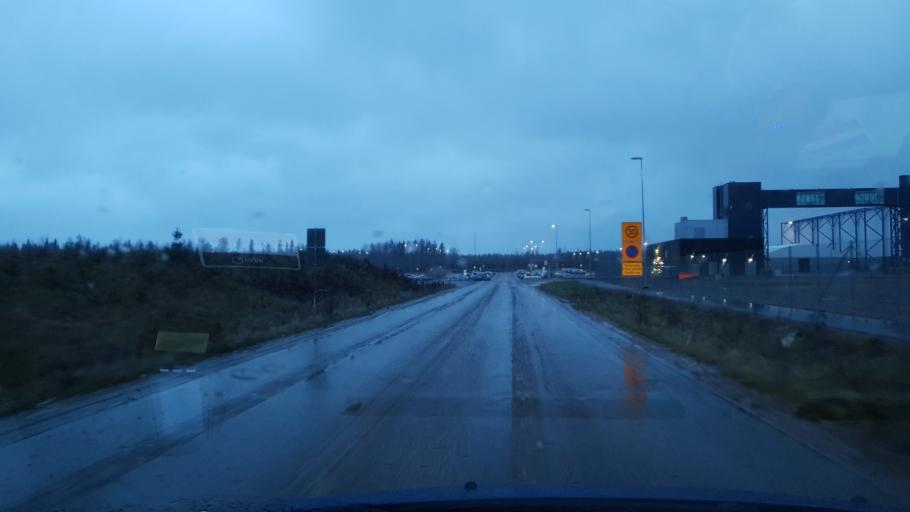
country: FI
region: Uusimaa
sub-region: Helsinki
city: Kerava
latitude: 60.3745
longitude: 25.1518
